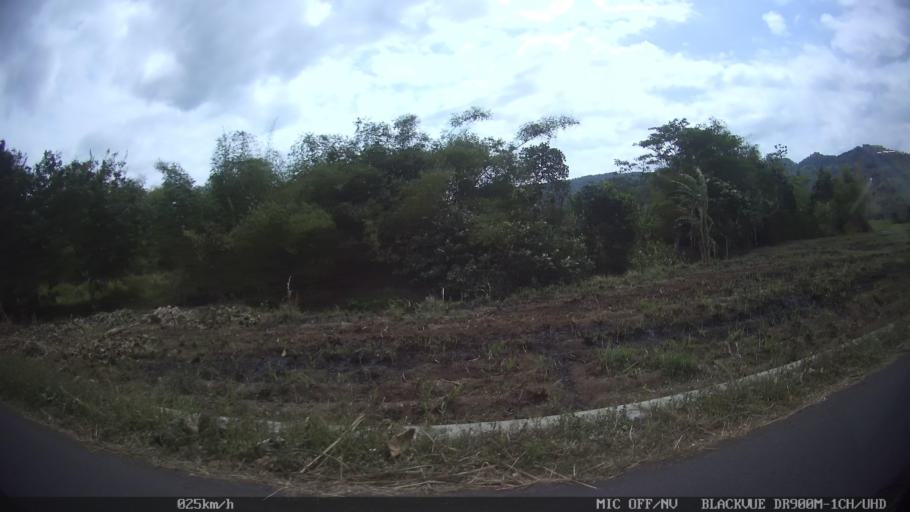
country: ID
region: Central Java
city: Candi Prambanan
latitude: -7.8111
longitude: 110.5040
